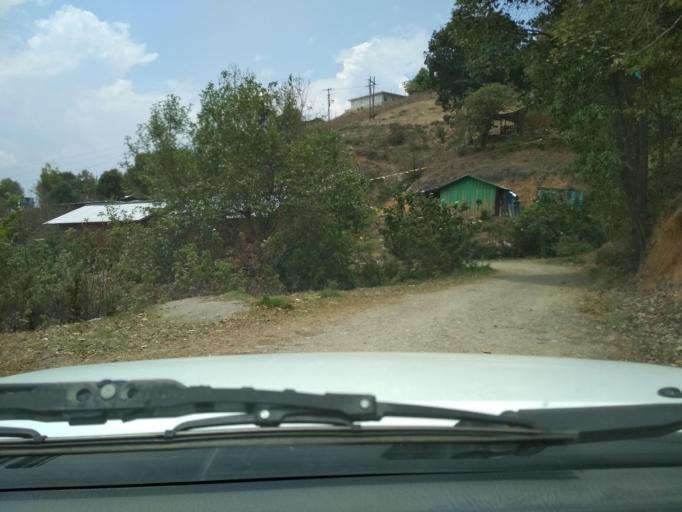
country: MX
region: Veracruz
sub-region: Acultzingo
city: Acatla
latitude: 18.7493
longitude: -97.1912
